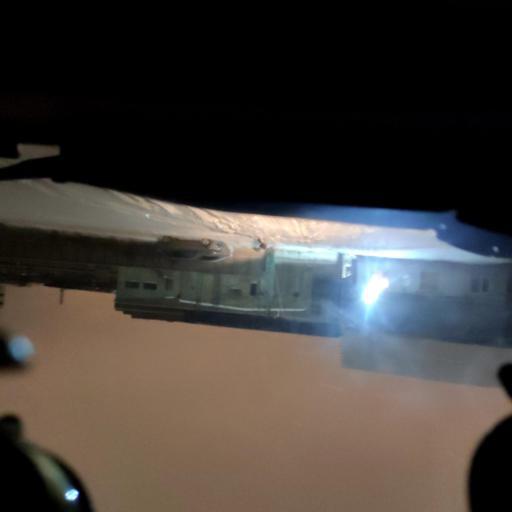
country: RU
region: Bashkortostan
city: Ufa
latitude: 54.8452
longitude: 56.1139
